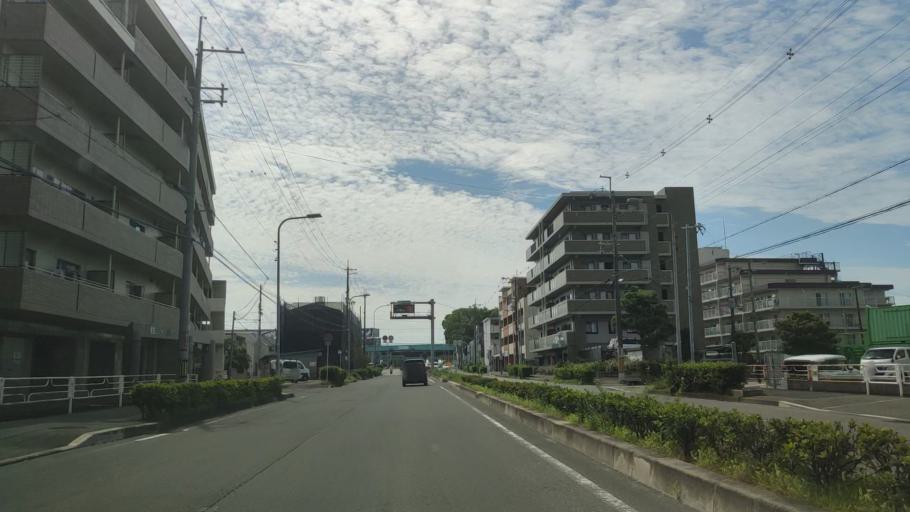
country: JP
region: Osaka
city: Ikeda
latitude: 34.8039
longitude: 135.4405
